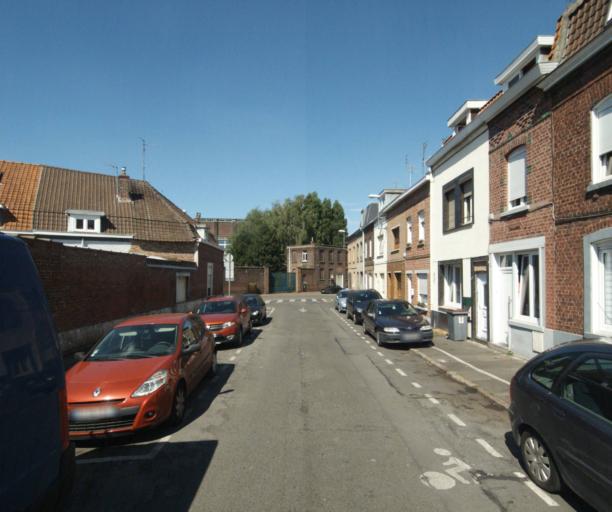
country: FR
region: Nord-Pas-de-Calais
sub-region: Departement du Nord
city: Tourcoing
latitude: 50.7244
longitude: 3.1796
